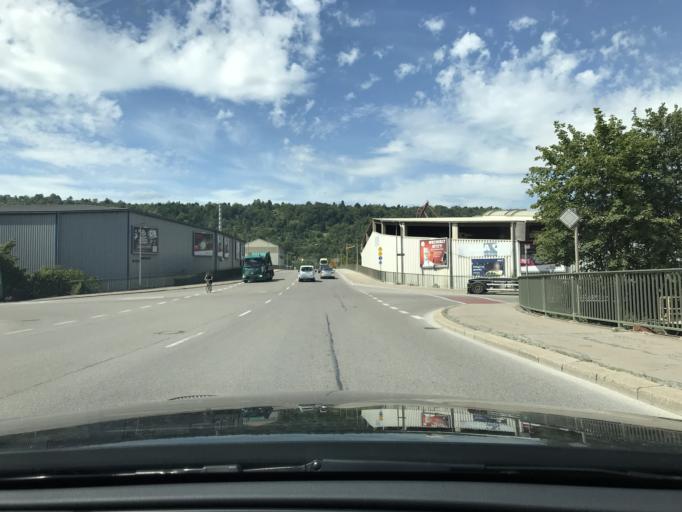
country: DE
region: Baden-Wuerttemberg
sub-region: Regierungsbezirk Stuttgart
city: Ostfildern
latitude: 48.7707
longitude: 9.2550
